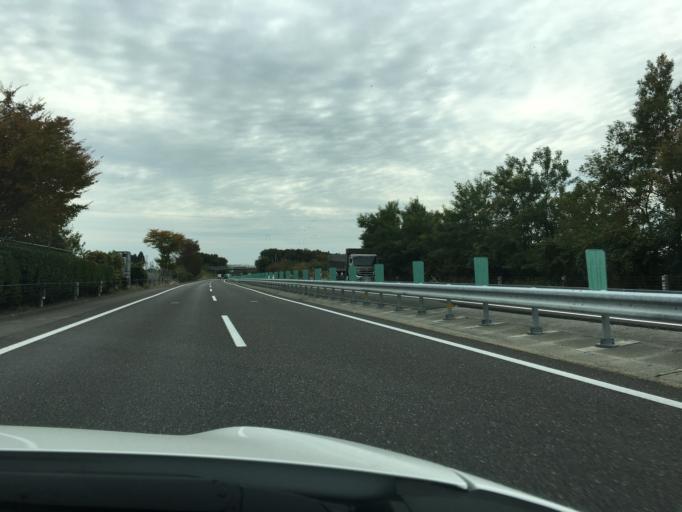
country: JP
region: Fukushima
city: Sukagawa
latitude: 37.2762
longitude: 140.3506
